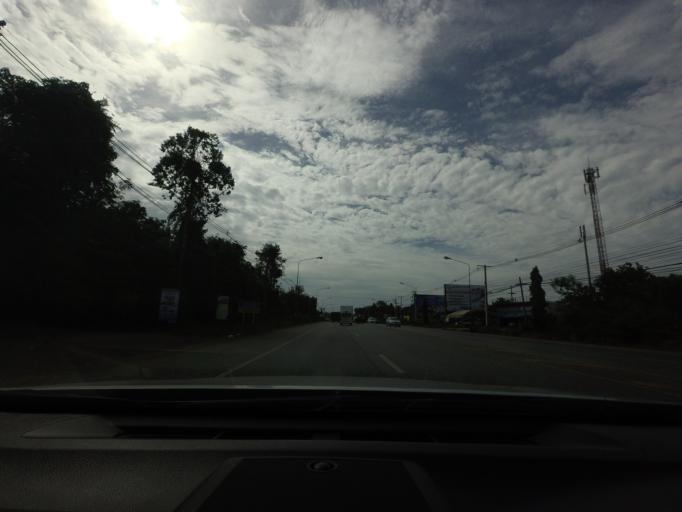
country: TH
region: Songkhla
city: Hat Yai
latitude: 6.9745
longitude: 100.4281
